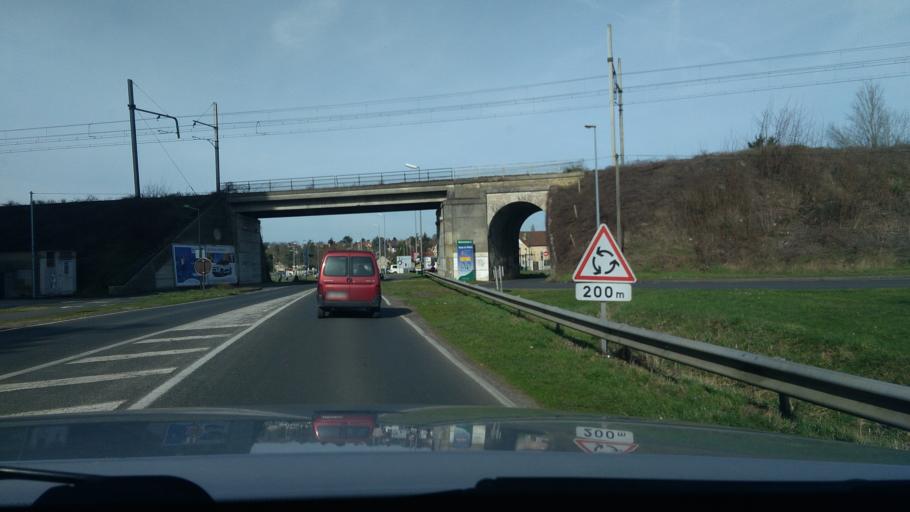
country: FR
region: Ile-de-France
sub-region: Departement de Seine-et-Marne
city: Livry-sur-Seine
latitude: 48.5174
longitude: 2.6734
